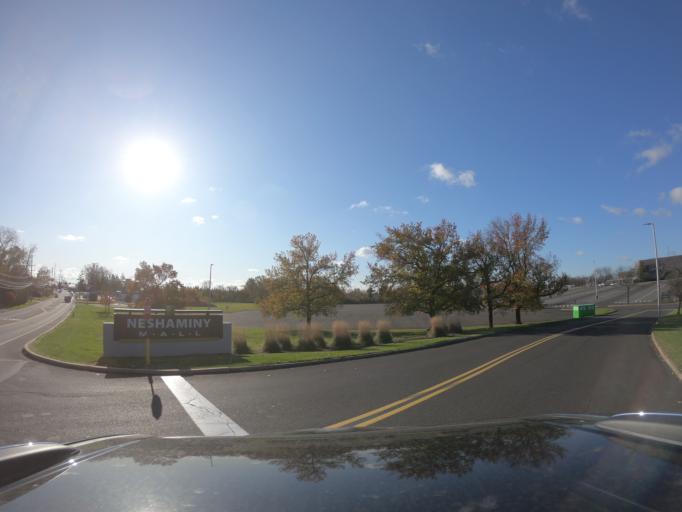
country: US
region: Pennsylvania
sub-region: Bucks County
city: Trevose
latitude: 40.1400
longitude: -74.9503
